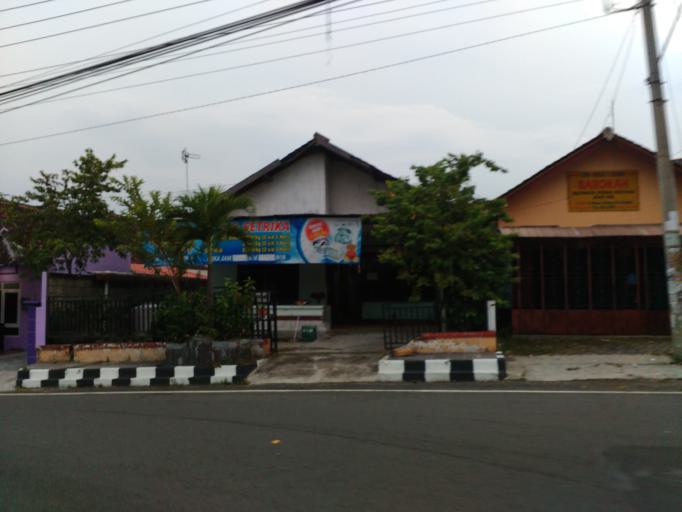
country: ID
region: Central Java
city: Boyolali
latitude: -7.5343
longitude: 110.6025
